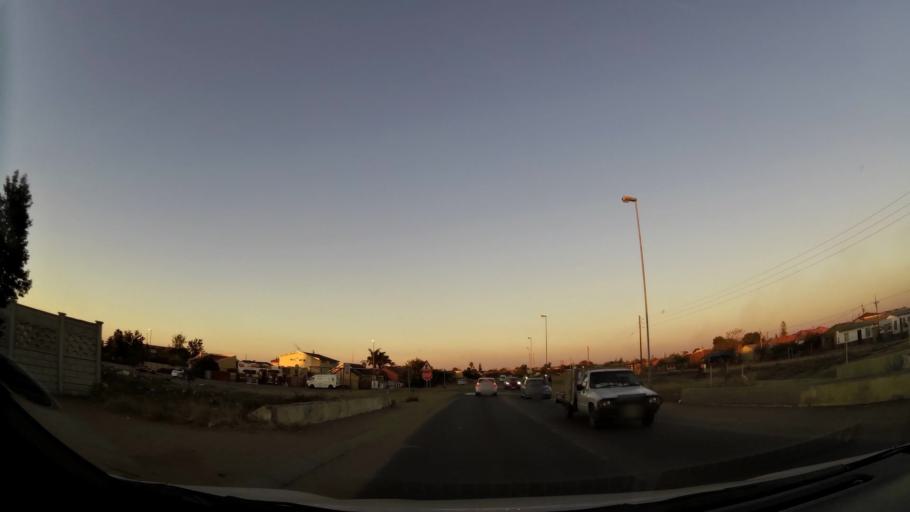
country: ZA
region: Limpopo
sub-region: Capricorn District Municipality
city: Polokwane
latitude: -23.8531
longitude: 29.3698
